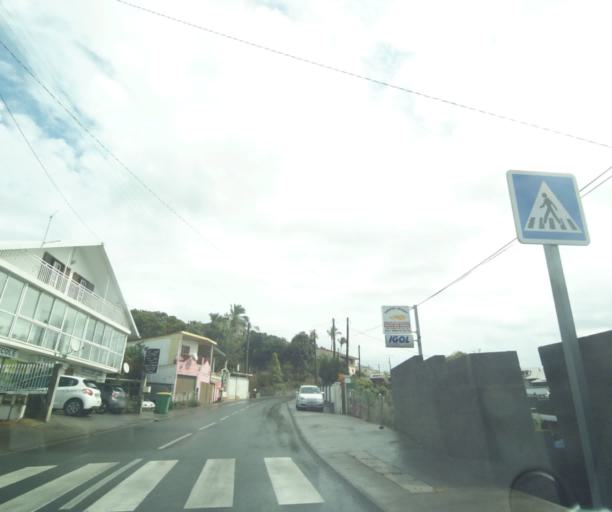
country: RE
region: Reunion
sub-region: Reunion
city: Saint-Paul
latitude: -21.0024
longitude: 55.3238
